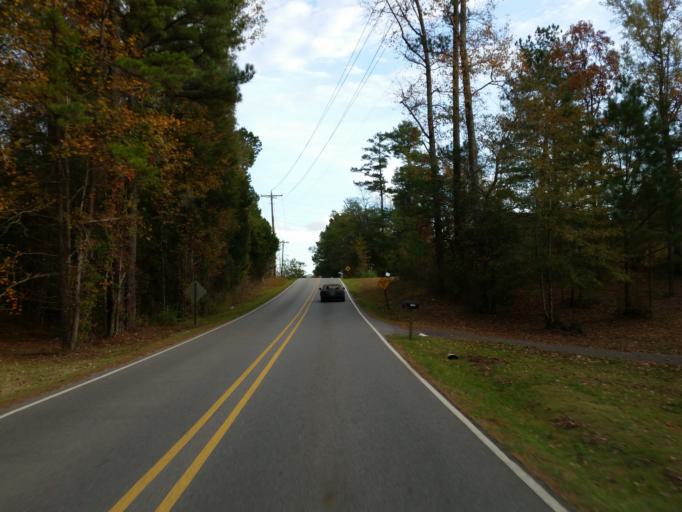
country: US
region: Mississippi
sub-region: Lauderdale County
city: Marion
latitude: 32.4064
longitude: -88.6034
